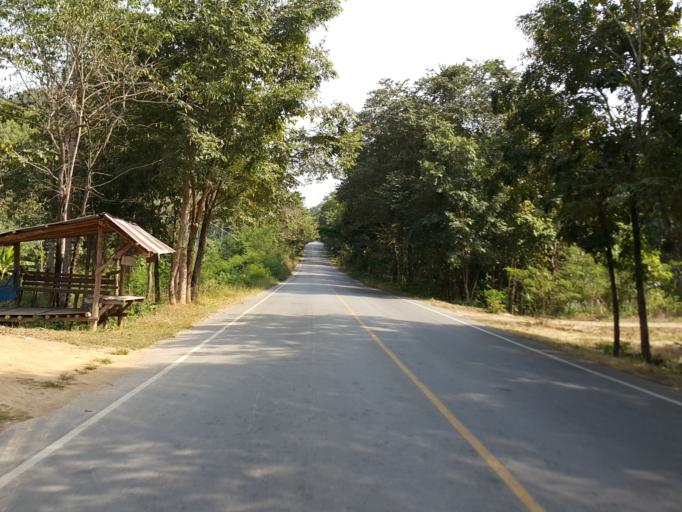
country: TH
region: Sukhothai
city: Thung Saliam
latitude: 17.3435
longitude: 99.4506
